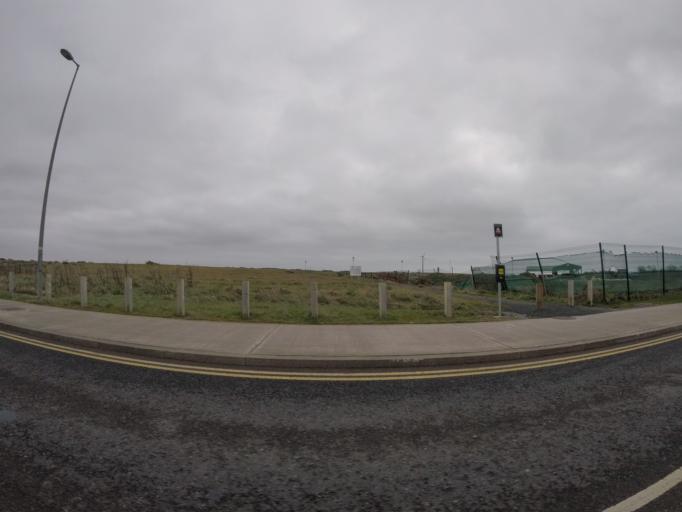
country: IE
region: Munster
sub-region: Waterford
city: Tra Mhor
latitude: 52.1615
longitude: -7.1360
